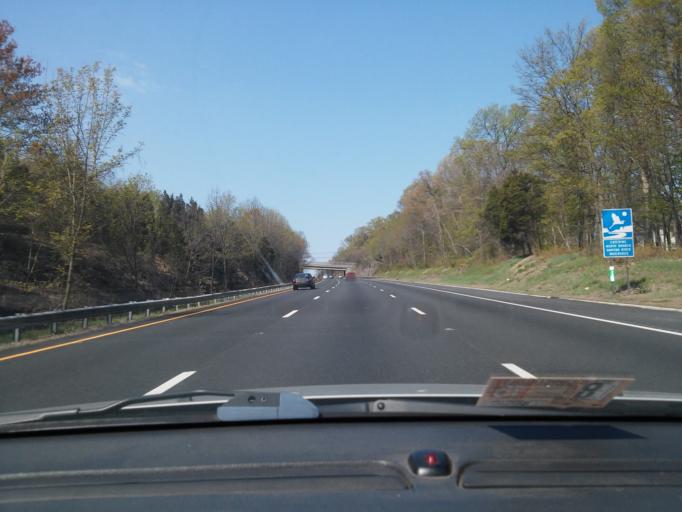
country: US
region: New Jersey
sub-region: Somerset County
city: Green Knoll
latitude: 40.6457
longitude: -74.5967
